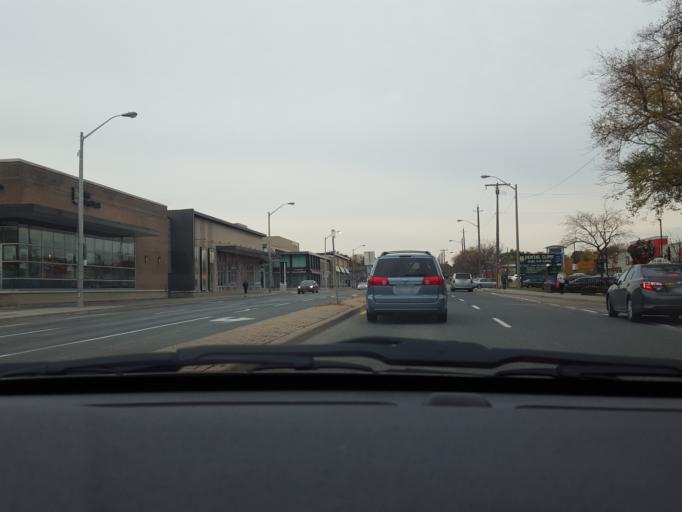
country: CA
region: Ontario
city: Willowdale
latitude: 43.7371
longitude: -79.3437
